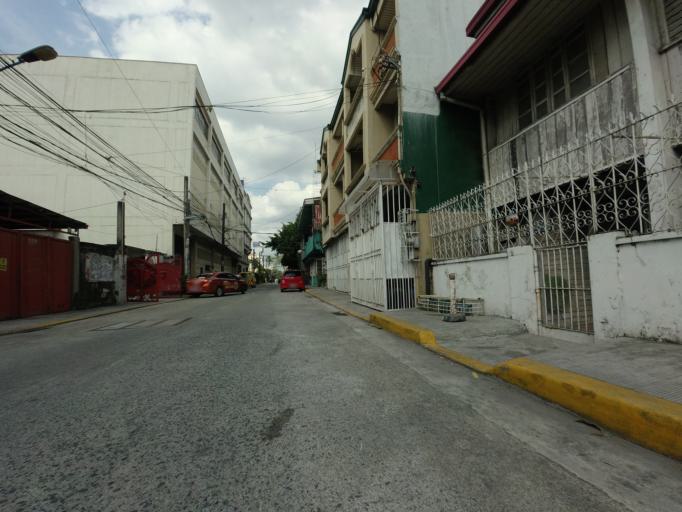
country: PH
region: Metro Manila
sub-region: City of Manila
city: Quiapo
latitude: 14.5710
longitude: 121.0030
